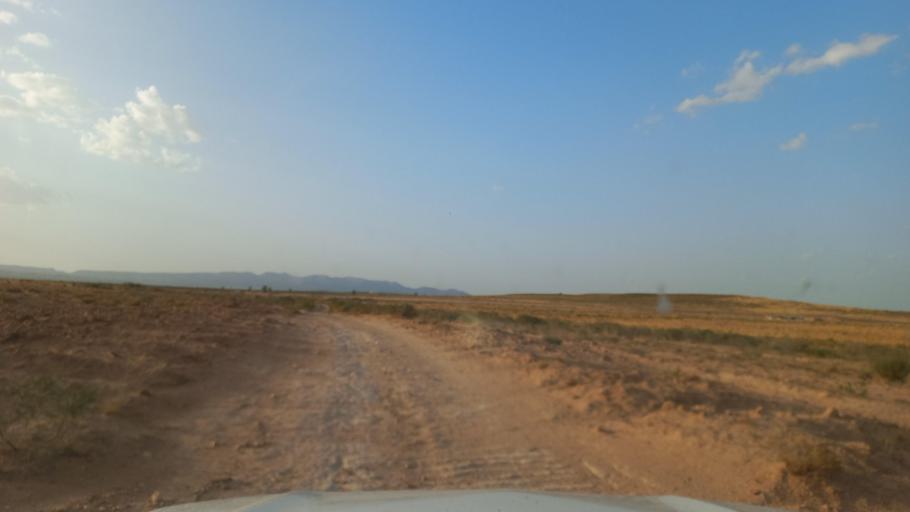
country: TN
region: Al Qasrayn
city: Sbiba
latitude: 35.3062
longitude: 9.0744
